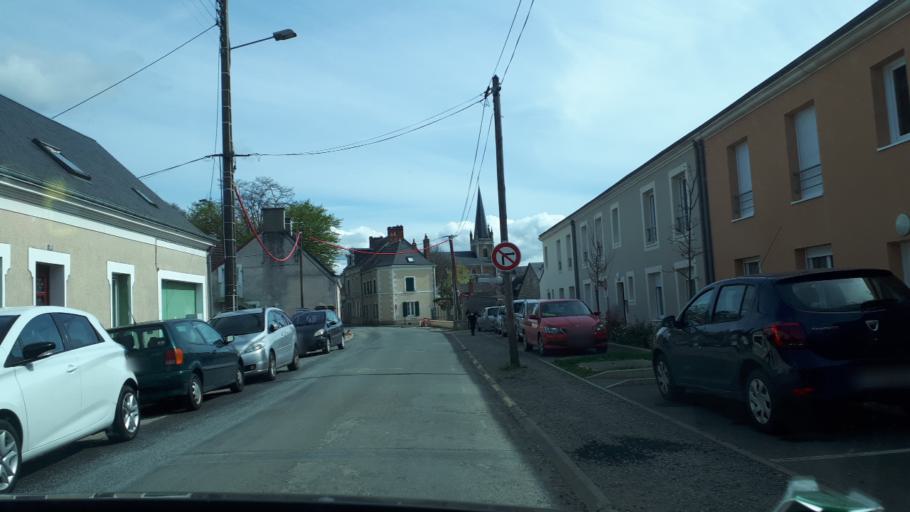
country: FR
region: Pays de la Loire
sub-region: Departement de la Sarthe
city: Ecommoy
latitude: 47.8277
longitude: 0.2703
